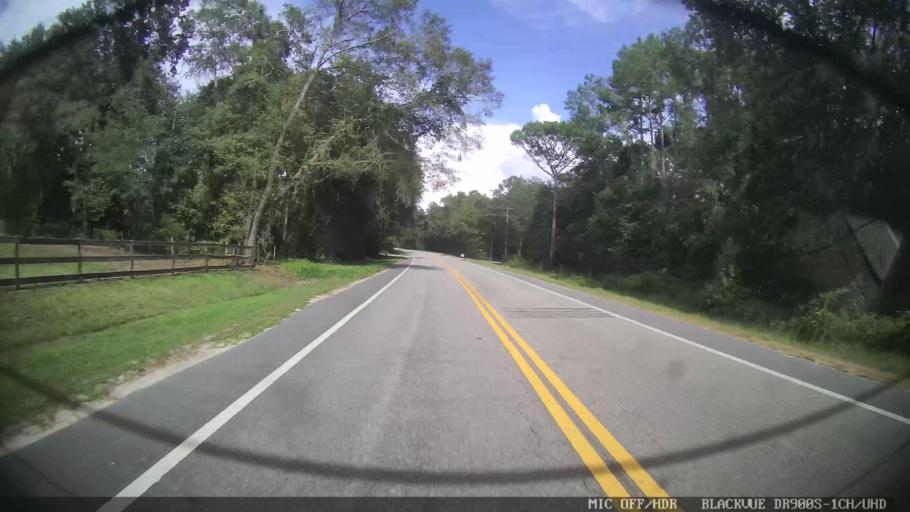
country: US
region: Florida
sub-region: Hamilton County
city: Jasper
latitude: 30.5541
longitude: -83.1072
